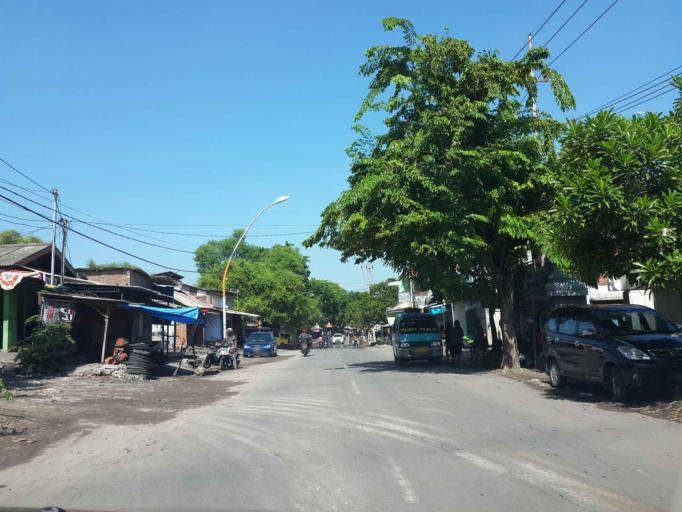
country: ID
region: East Java
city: Gresik
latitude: -7.1727
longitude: 112.6573
